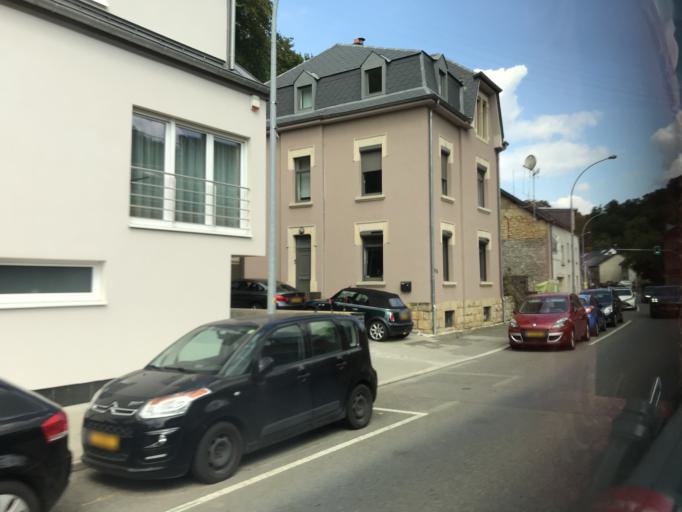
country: LU
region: Luxembourg
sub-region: Canton de Luxembourg
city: Hesperange
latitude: 49.5763
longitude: 6.1535
